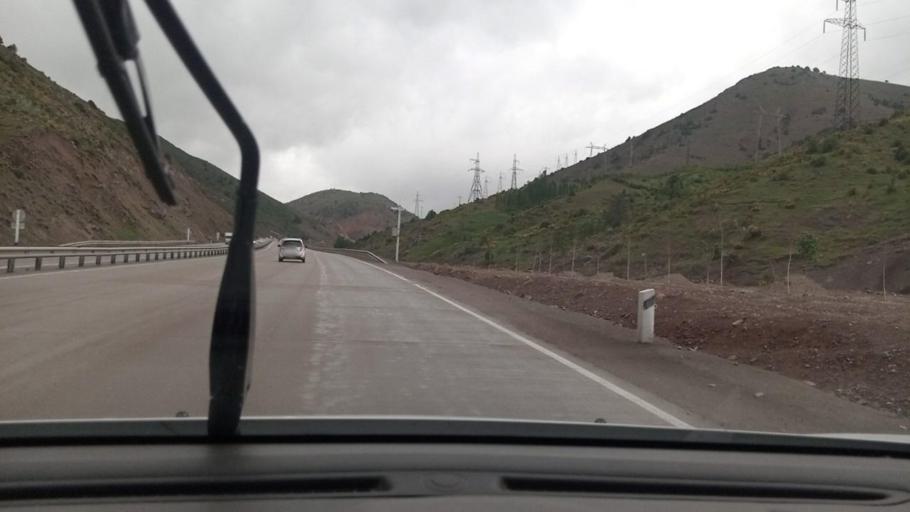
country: UZ
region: Toshkent
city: Angren
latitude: 41.0532
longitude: 70.5666
